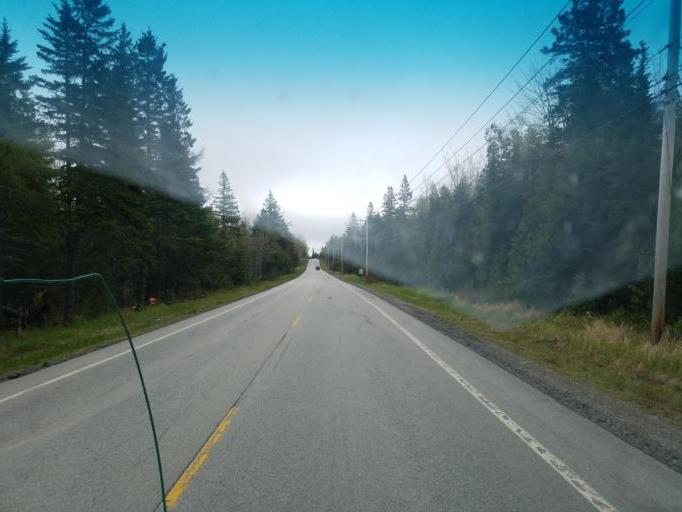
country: US
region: Maine
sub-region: Washington County
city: Eastport
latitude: 44.8013
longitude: -67.1330
